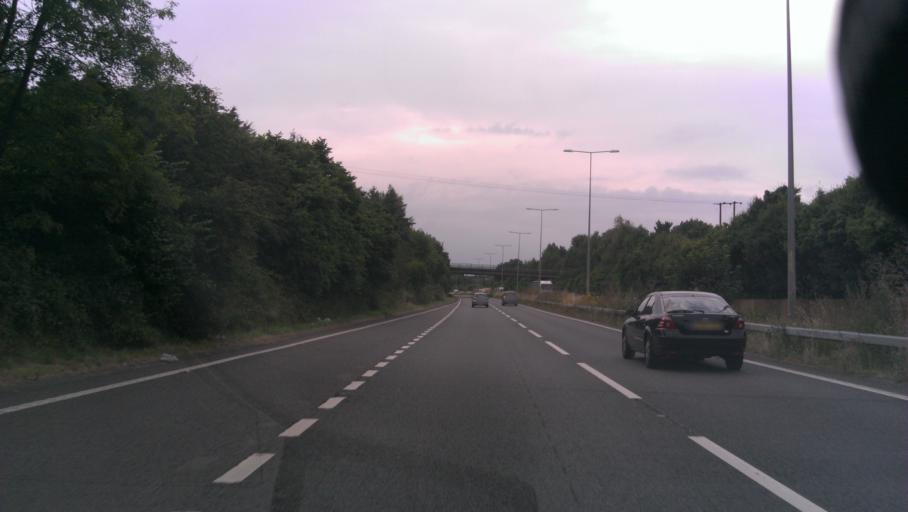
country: GB
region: England
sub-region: Kent
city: Blean
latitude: 51.2837
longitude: 1.0302
